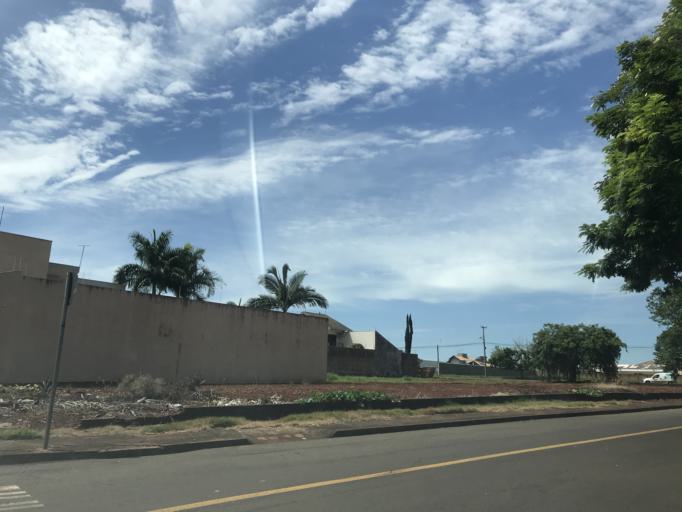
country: BR
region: Parana
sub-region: Londrina
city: Londrina
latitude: -23.3471
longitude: -51.1596
